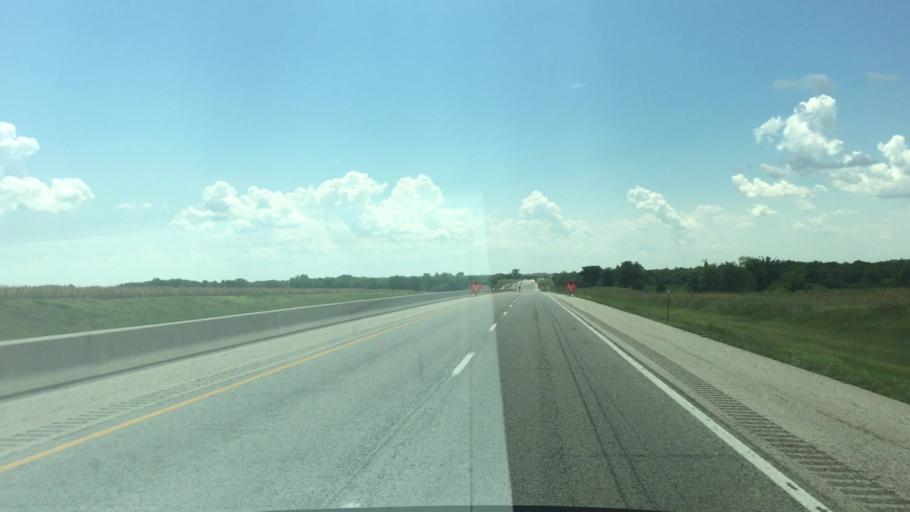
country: US
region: Kansas
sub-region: Shawnee County
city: Auburn
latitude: 38.7806
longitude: -95.9185
